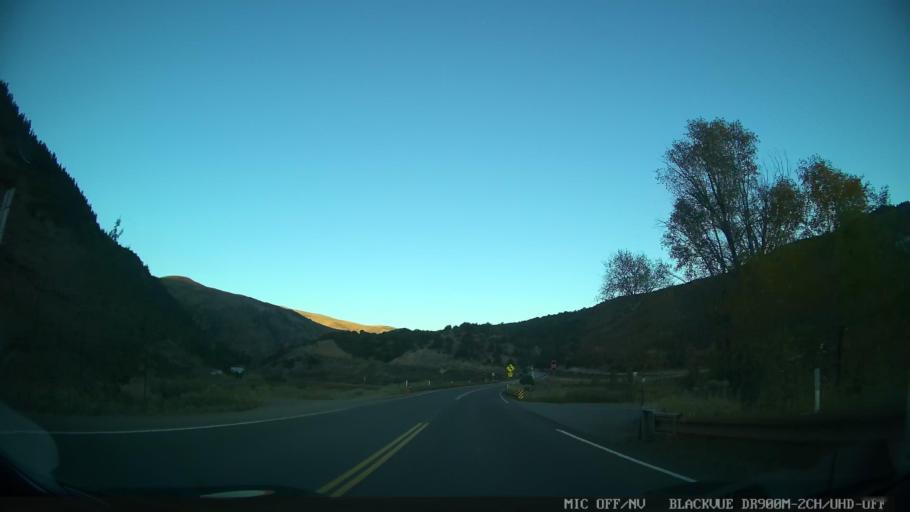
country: US
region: Colorado
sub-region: Eagle County
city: Edwards
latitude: 39.8563
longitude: -106.6479
